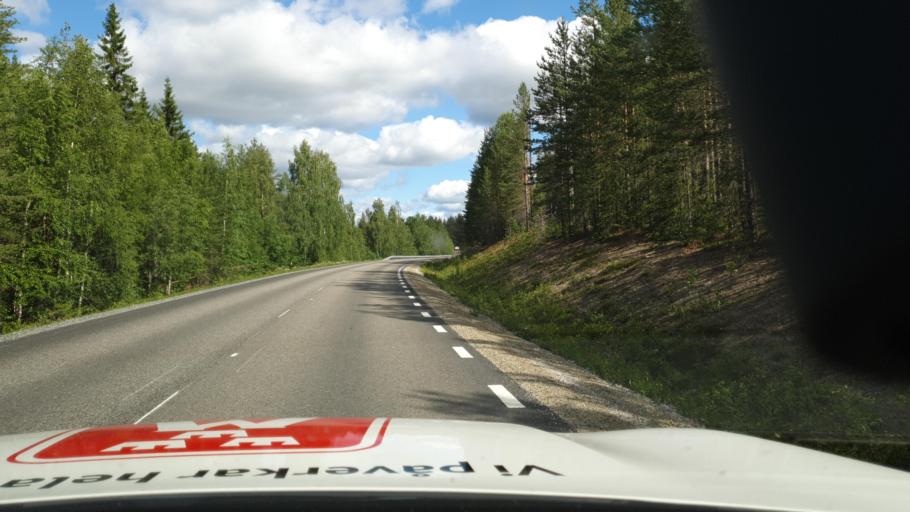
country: SE
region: Vaesterbotten
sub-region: Lycksele Kommun
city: Lycksele
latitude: 64.8646
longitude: 18.7210
